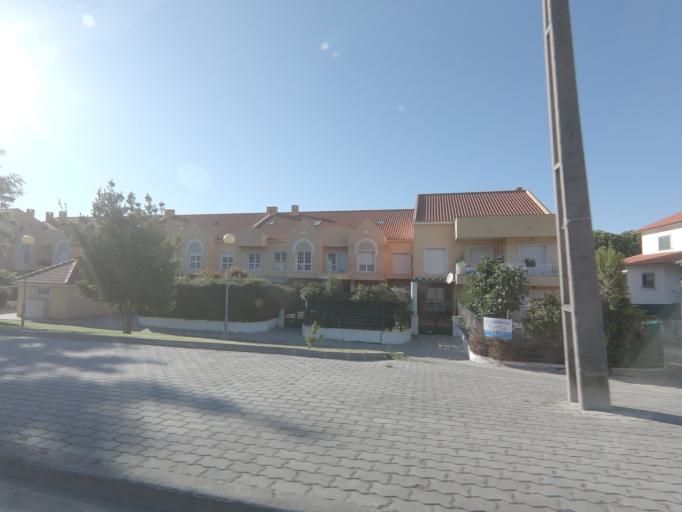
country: PT
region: Setubal
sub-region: Palmela
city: Quinta do Anjo
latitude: 38.5595
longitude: -8.9581
